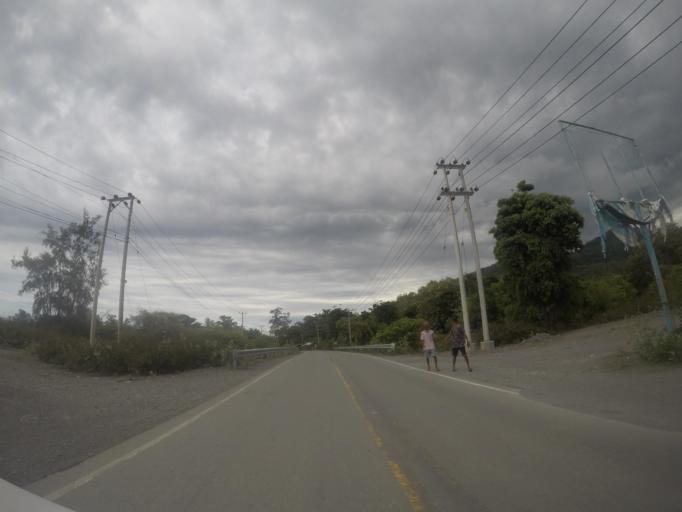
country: TL
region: Liquica
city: Liquica
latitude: -8.5845
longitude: 125.3535
